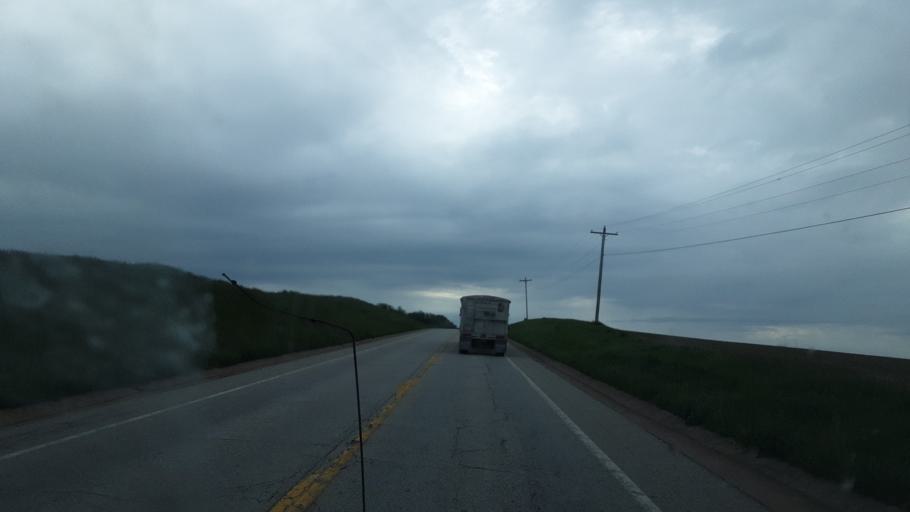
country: US
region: Illinois
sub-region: Fulton County
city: Lewistown
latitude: 40.3420
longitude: -90.2081
